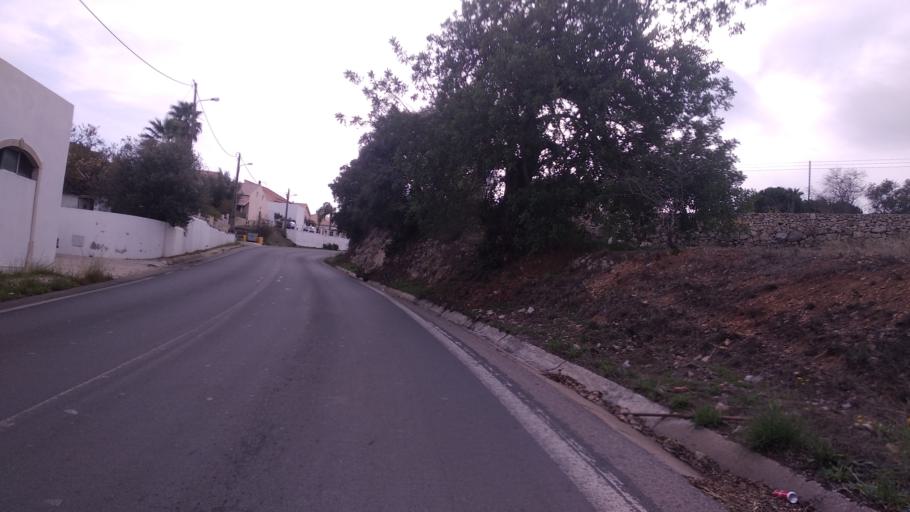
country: PT
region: Faro
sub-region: Loule
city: Loule
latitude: 37.1438
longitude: -7.9808
